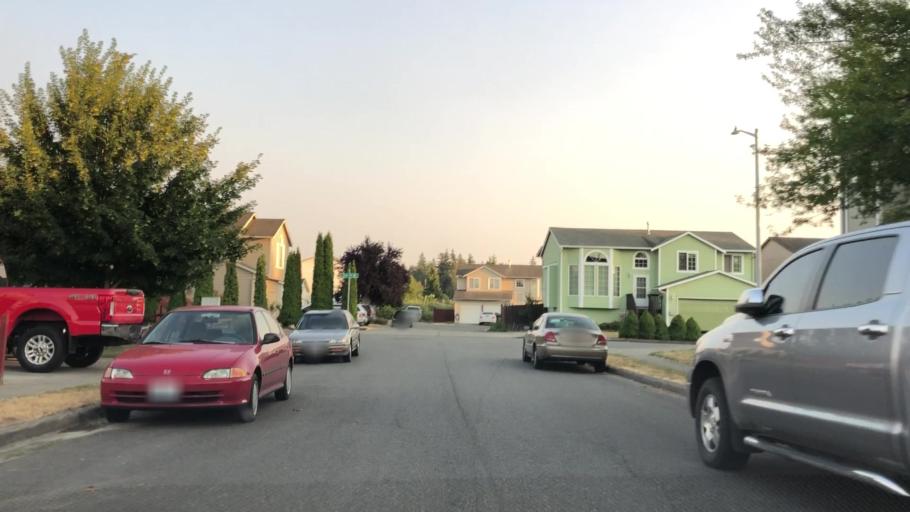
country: US
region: Washington
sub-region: Snohomish County
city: Marysville
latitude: 48.0902
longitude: -122.1530
